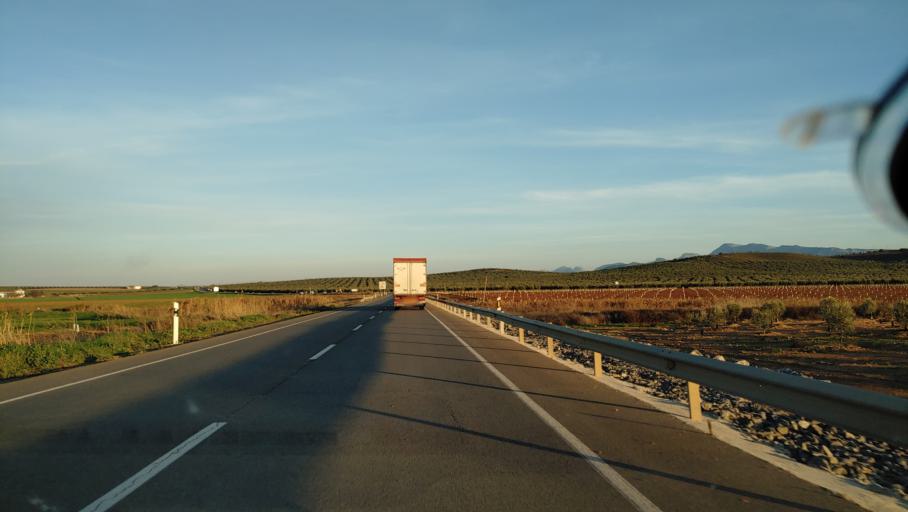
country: ES
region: Andalusia
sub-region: Provincia de Malaga
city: Humilladero
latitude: 37.0528
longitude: -4.7610
